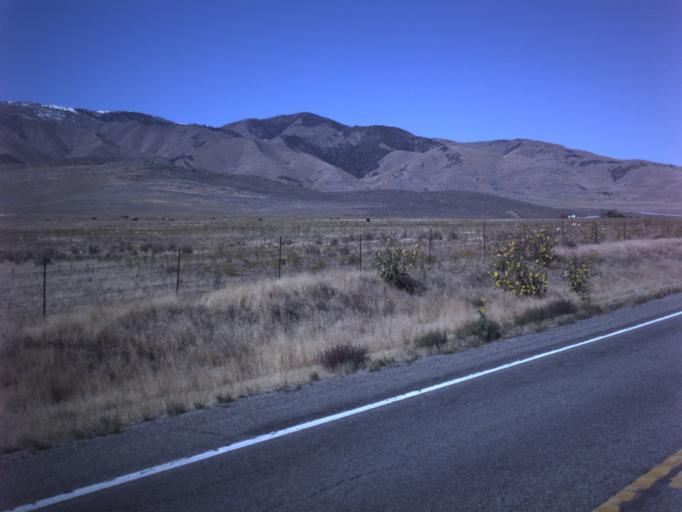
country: US
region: Utah
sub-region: Tooele County
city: Grantsville
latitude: 40.6306
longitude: -112.5133
